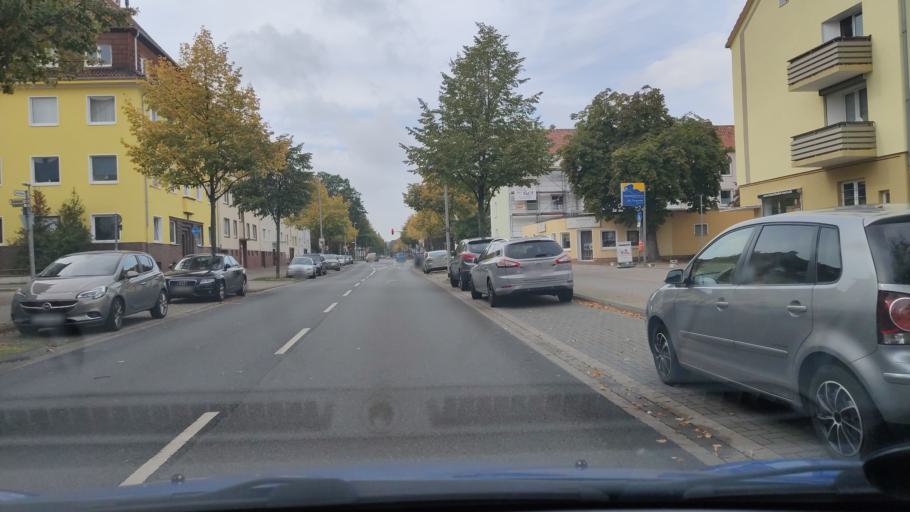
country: DE
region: Lower Saxony
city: Ronnenberg
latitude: 52.3586
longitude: 9.6727
